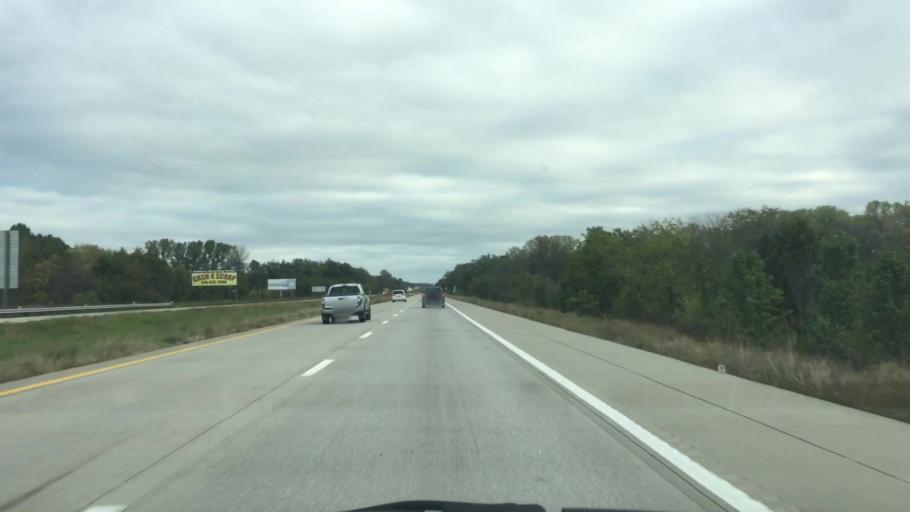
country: US
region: Missouri
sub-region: Clay County
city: Kearney
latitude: 39.3852
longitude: -94.3628
